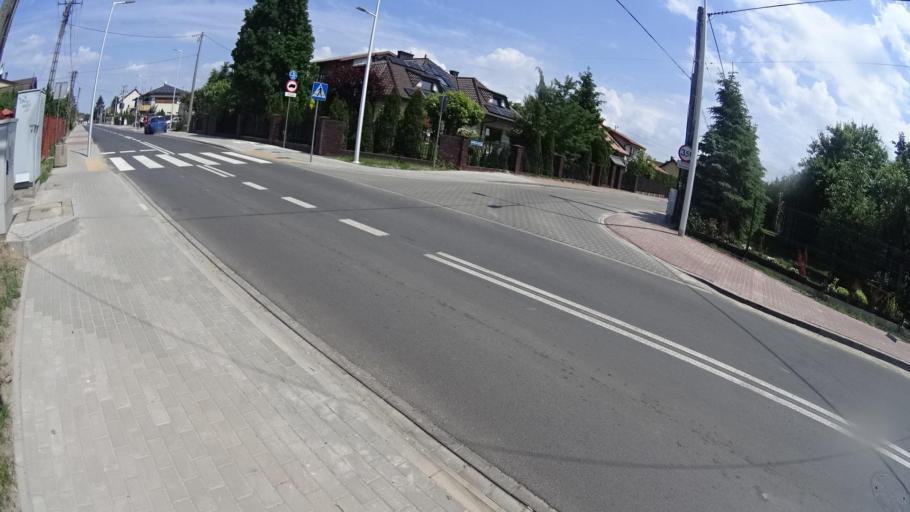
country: PL
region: Masovian Voivodeship
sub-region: Powiat warszawski zachodni
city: Stare Babice
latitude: 52.2568
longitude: 20.8380
